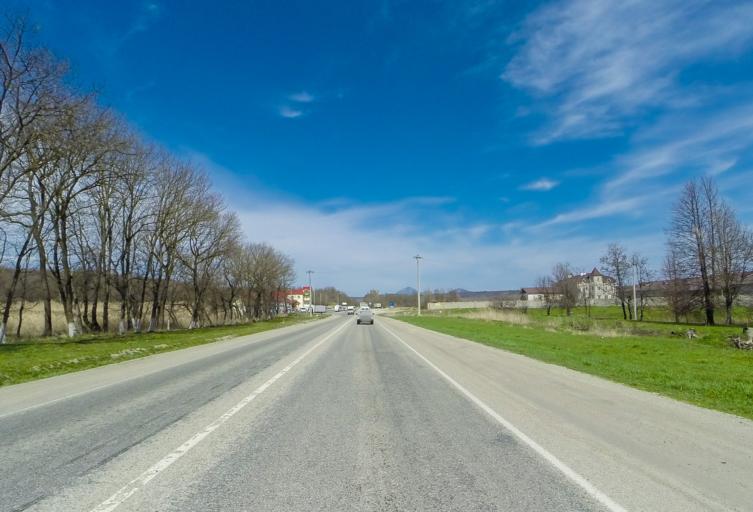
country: RU
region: Kabardino-Balkariya
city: Zalukokoazhe
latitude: 43.9509
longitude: 43.1574
